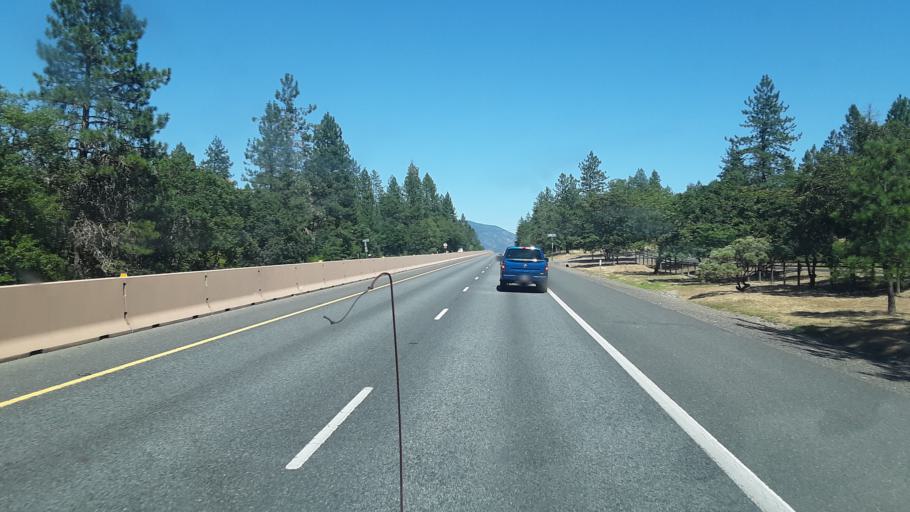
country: US
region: Oregon
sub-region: Josephine County
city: Redwood
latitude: 42.4135
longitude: -123.4038
